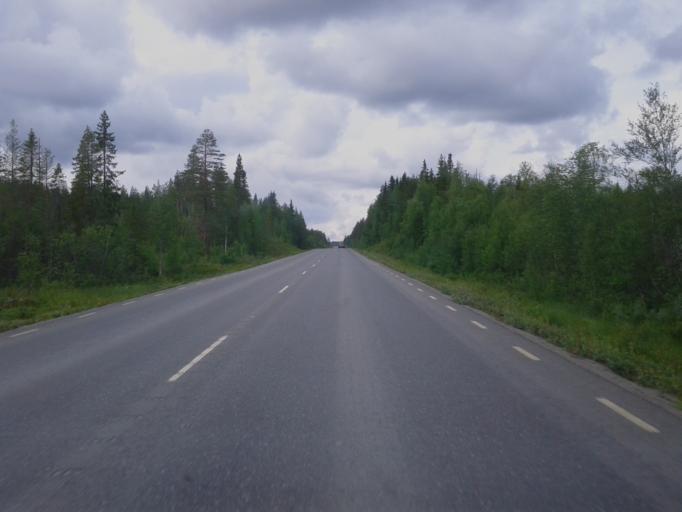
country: SE
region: Vaesterbotten
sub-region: Norsjo Kommun
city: Norsjoe
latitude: 64.9874
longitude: 19.4558
